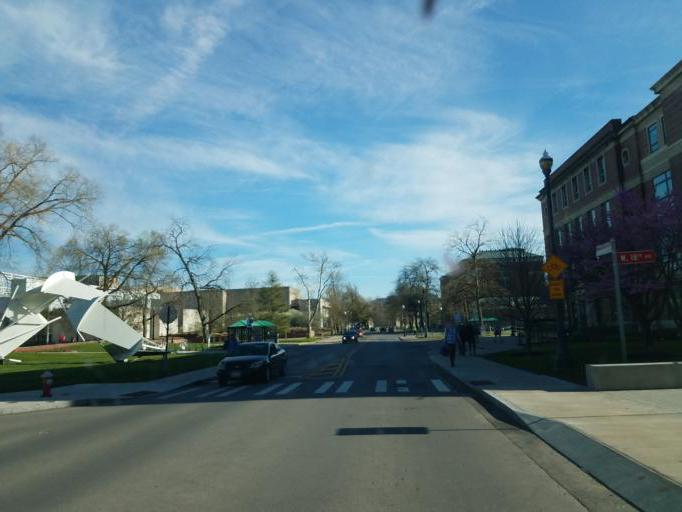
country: US
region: Ohio
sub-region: Franklin County
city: Grandview Heights
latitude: 40.0024
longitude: -83.0108
